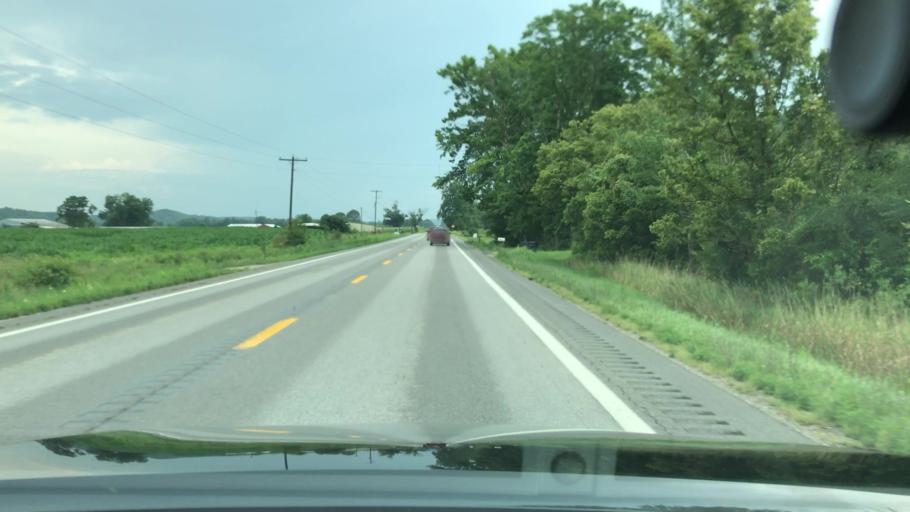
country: US
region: West Virginia
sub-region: Putnam County
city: Buffalo
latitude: 38.7083
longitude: -81.9672
